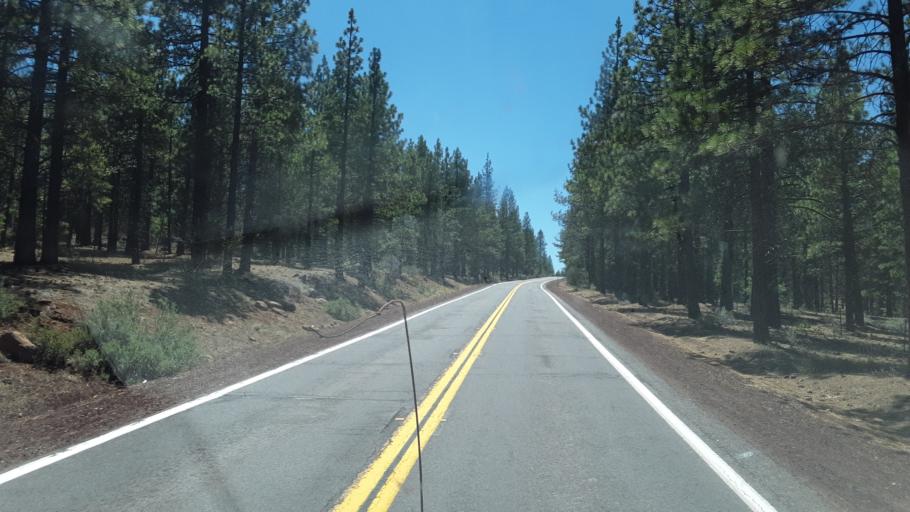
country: US
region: California
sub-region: Lassen County
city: Johnstonville
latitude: 40.4792
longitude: -120.5466
